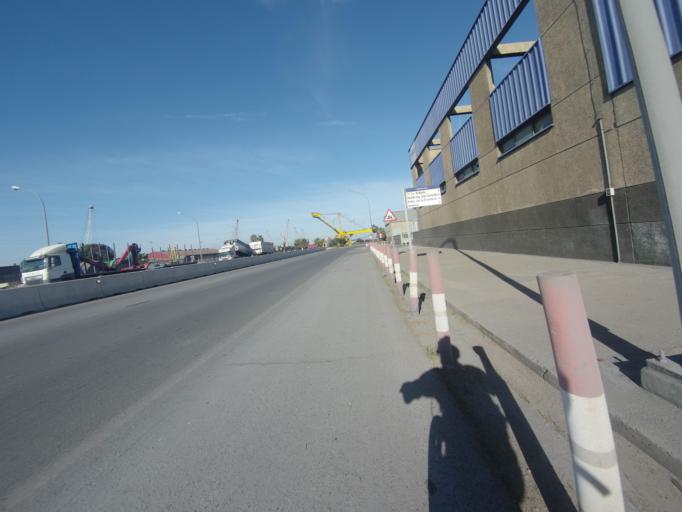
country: ES
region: Andalusia
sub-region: Provincia de Huelva
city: Punta Umbria
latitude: 37.1904
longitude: -6.9296
